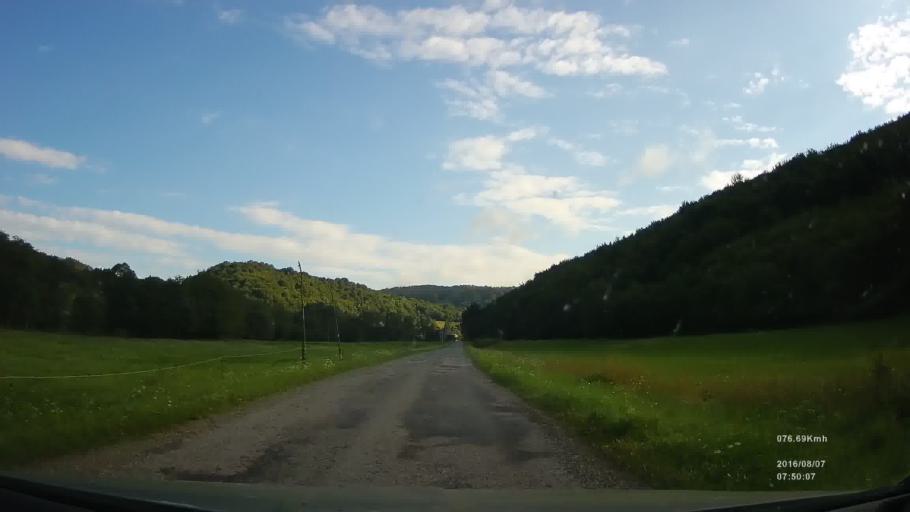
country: SK
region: Presovsky
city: Medzilaborce
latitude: 49.2958
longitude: 21.7760
